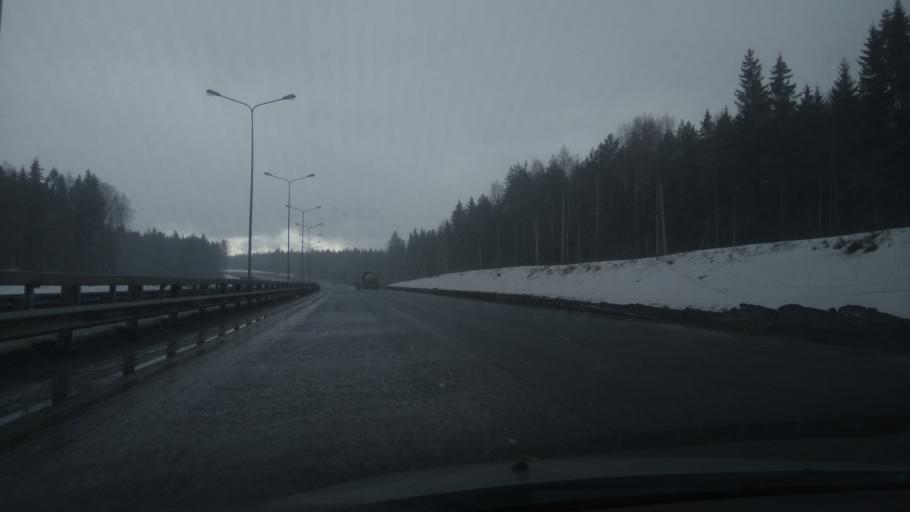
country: RU
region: Perm
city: Zvezdnyy
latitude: 57.7519
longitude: 56.3332
